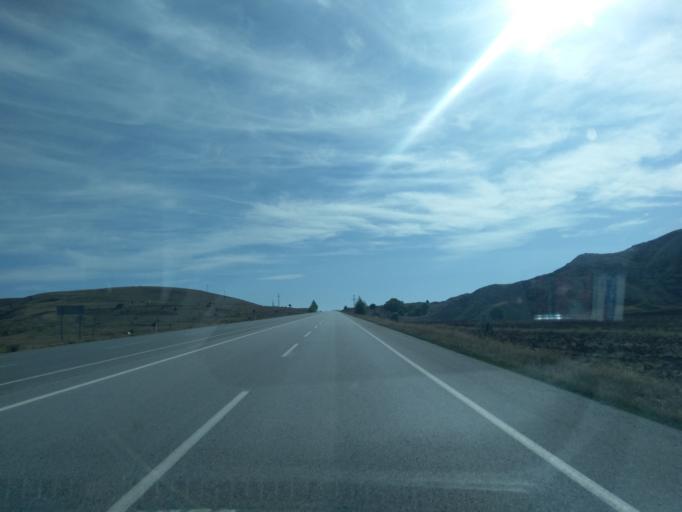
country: TR
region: Sivas
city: Imranli
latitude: 39.8843
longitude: 38.0374
